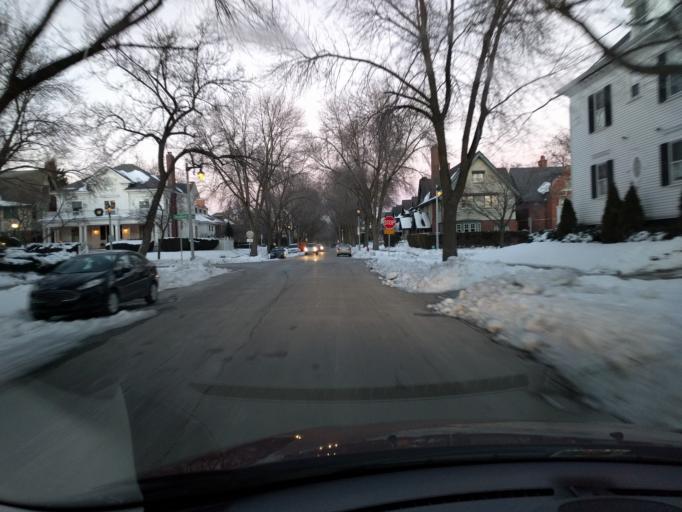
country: US
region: Wisconsin
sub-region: Milwaukee County
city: Shorewood
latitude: 43.0623
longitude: -87.8767
